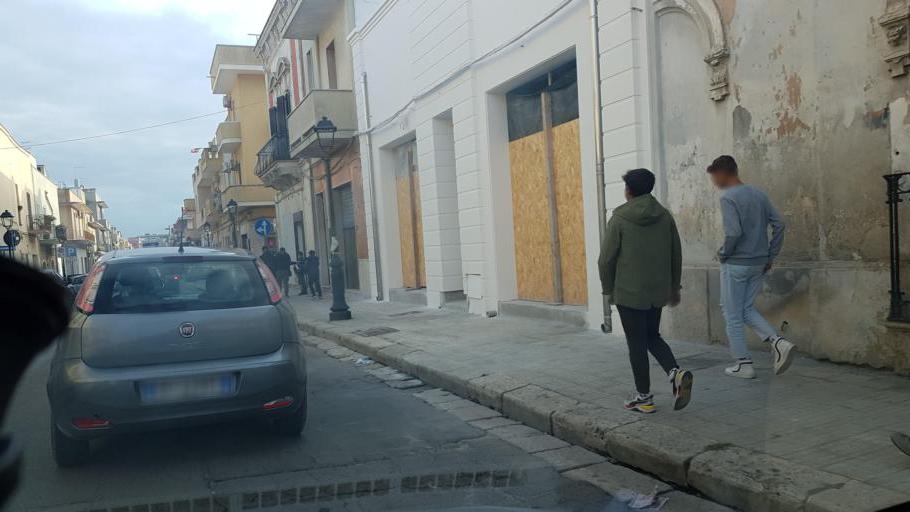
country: IT
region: Apulia
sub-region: Provincia di Brindisi
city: Francavilla Fontana
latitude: 40.5320
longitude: 17.5776
